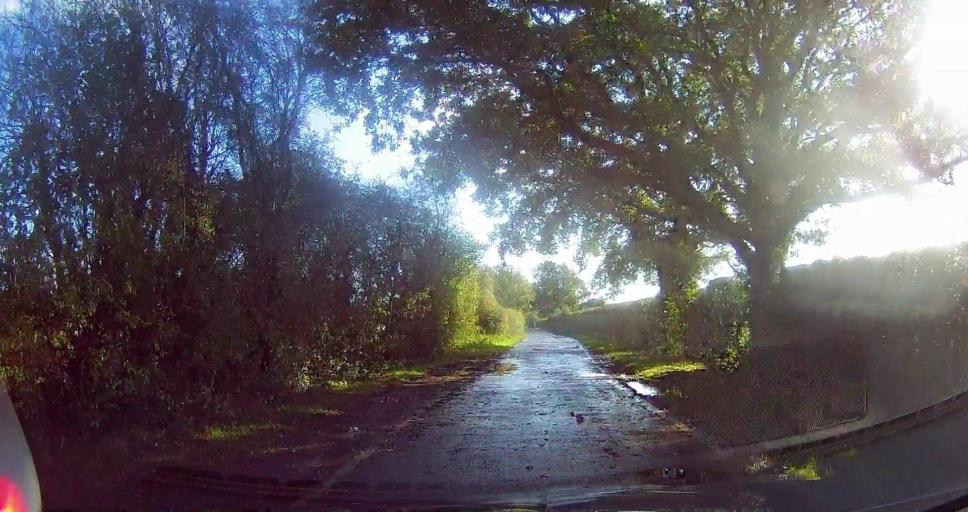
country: GB
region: England
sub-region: Staffordshire
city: Whittington
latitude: 52.6904
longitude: -1.7776
